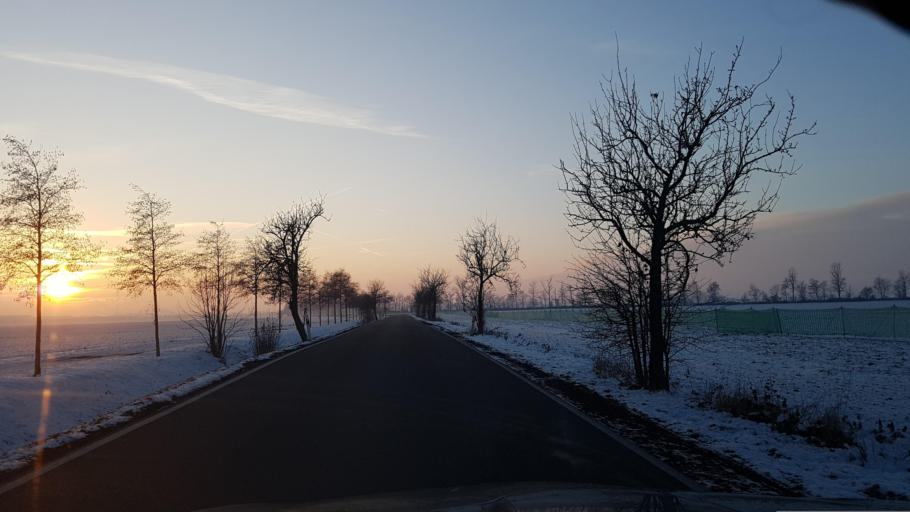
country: DE
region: Saxony
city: Taucha
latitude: 51.4246
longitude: 12.4746
